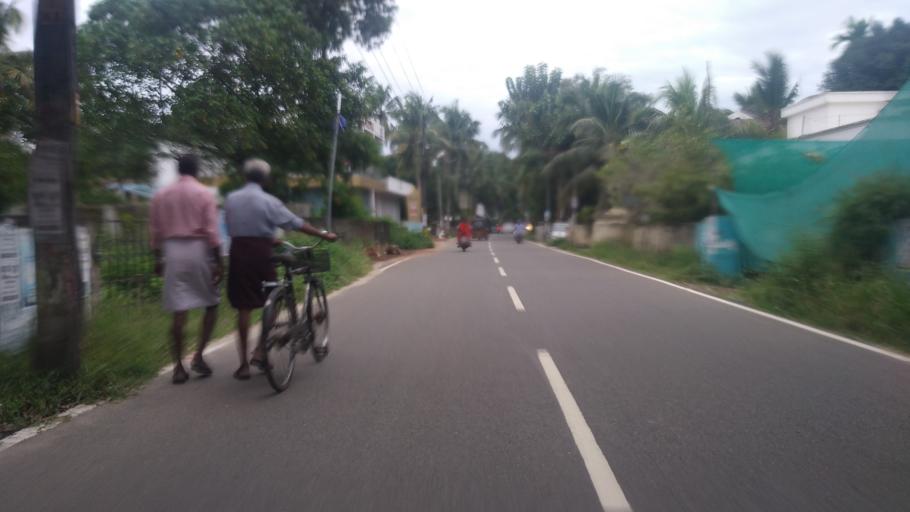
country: IN
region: Kerala
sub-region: Alappuzha
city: Arukutti
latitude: 9.8669
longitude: 76.2915
